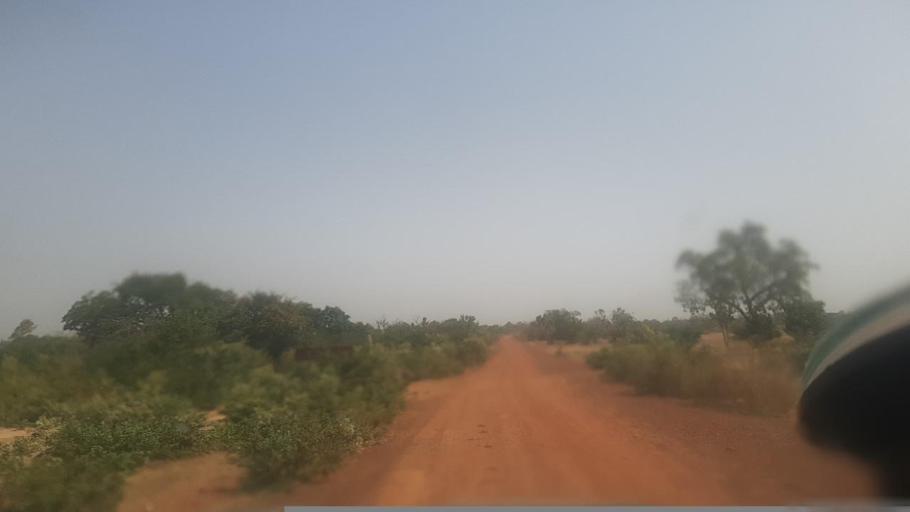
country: ML
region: Segou
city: Segou
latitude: 12.9316
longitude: -6.2846
